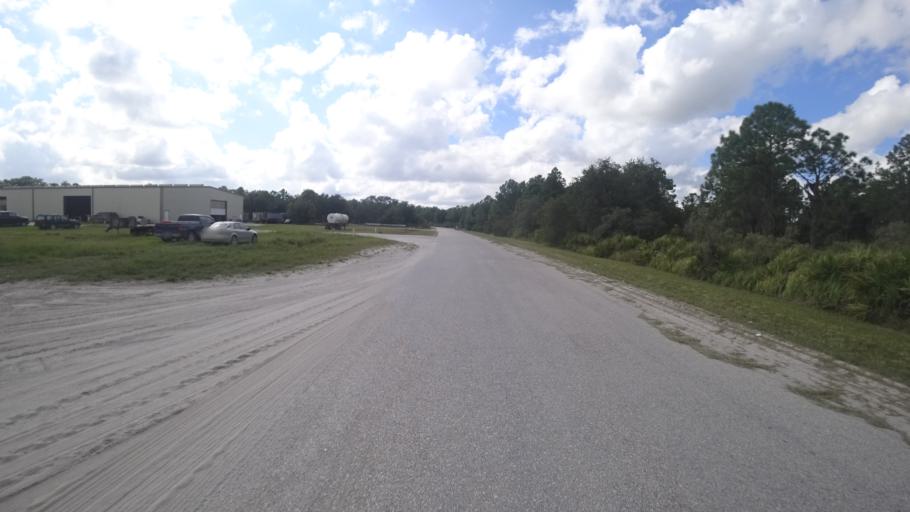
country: US
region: Florida
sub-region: Hillsborough County
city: Wimauma
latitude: 27.4572
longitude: -82.1835
